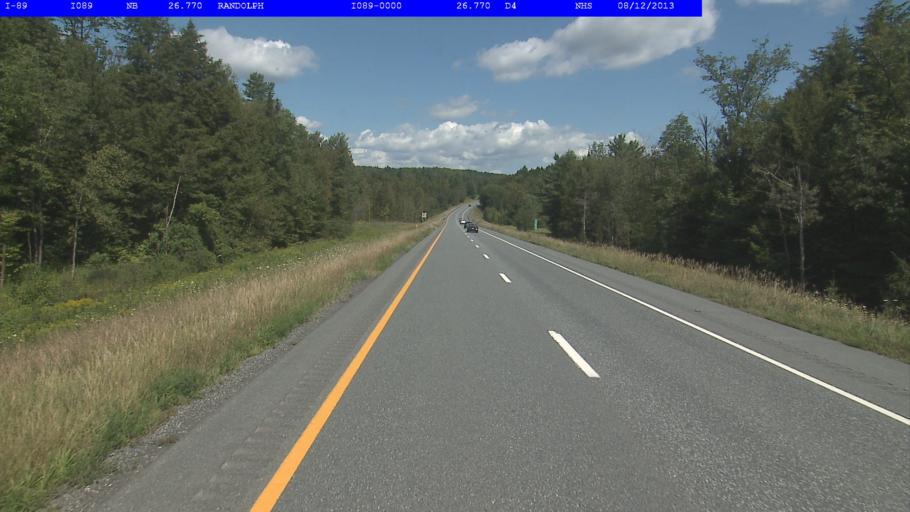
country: US
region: Vermont
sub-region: Orange County
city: Randolph
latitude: 43.8859
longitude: -72.6160
